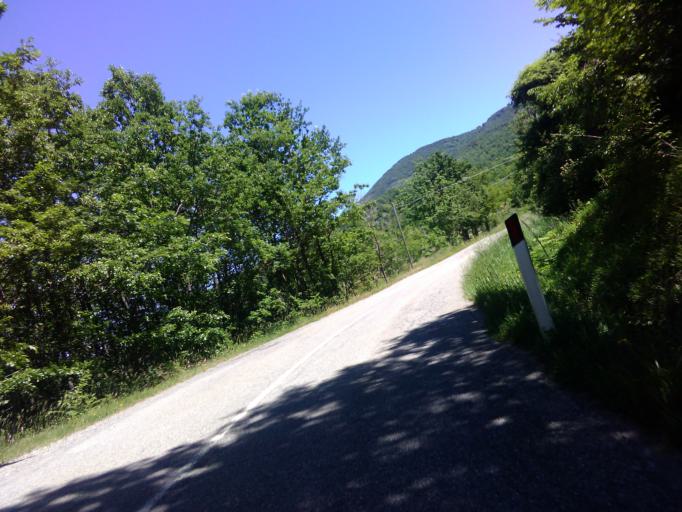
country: IT
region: Emilia-Romagna
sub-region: Provincia di Parma
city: Berceto
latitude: 44.5299
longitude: 10.0311
